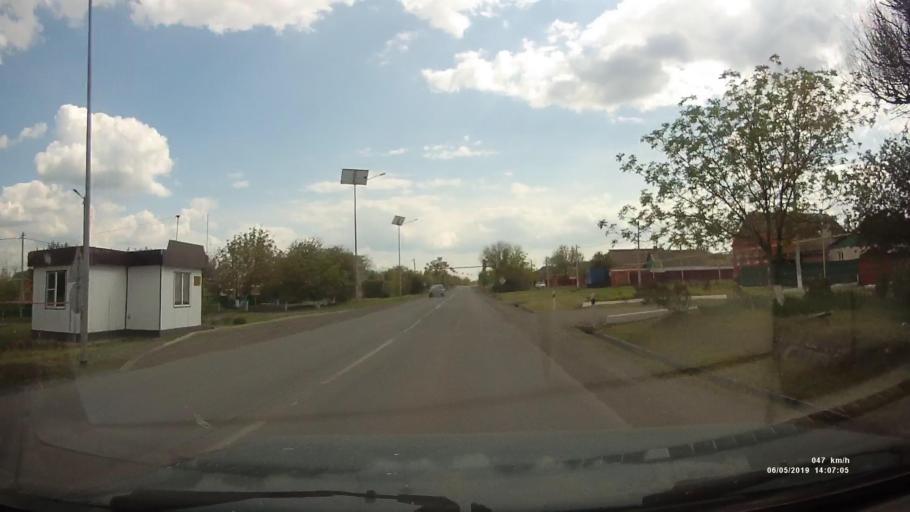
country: RU
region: Rostov
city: Shakhty
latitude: 47.6838
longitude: 40.3029
